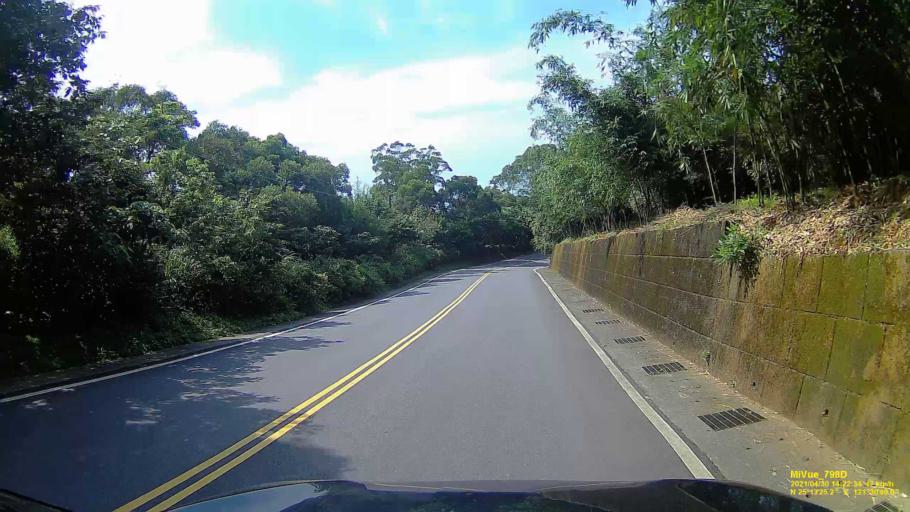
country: TW
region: Taipei
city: Taipei
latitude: 25.2239
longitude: 121.5137
